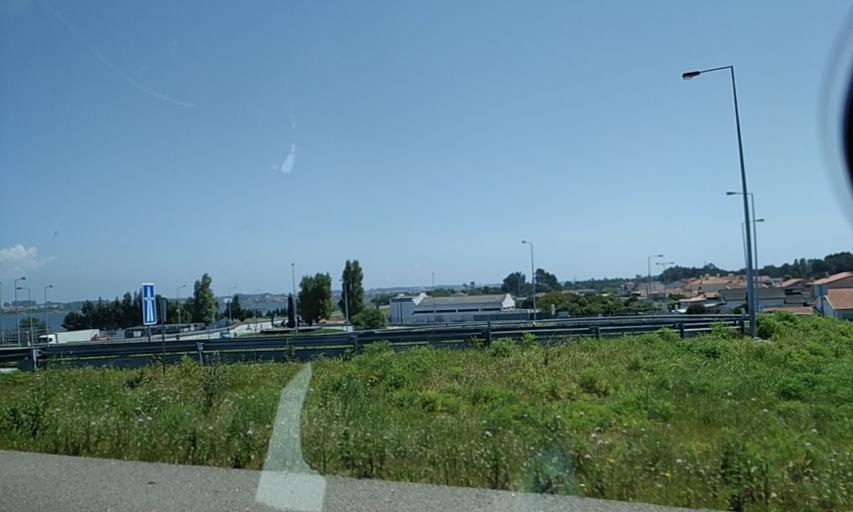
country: PT
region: Aveiro
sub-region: Ilhavo
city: Gafanha da Nazare
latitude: 40.6313
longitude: -8.6899
